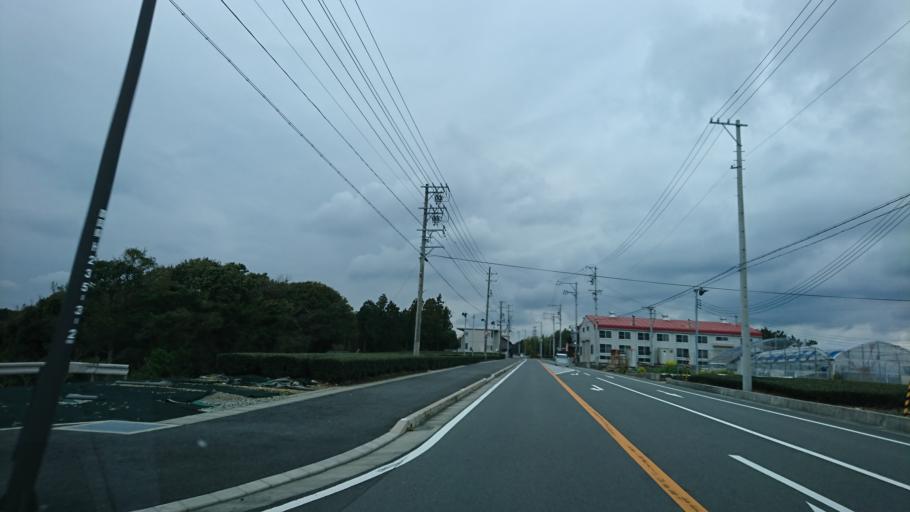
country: JP
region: Shizuoka
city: Shimada
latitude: 34.7520
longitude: 138.1708
